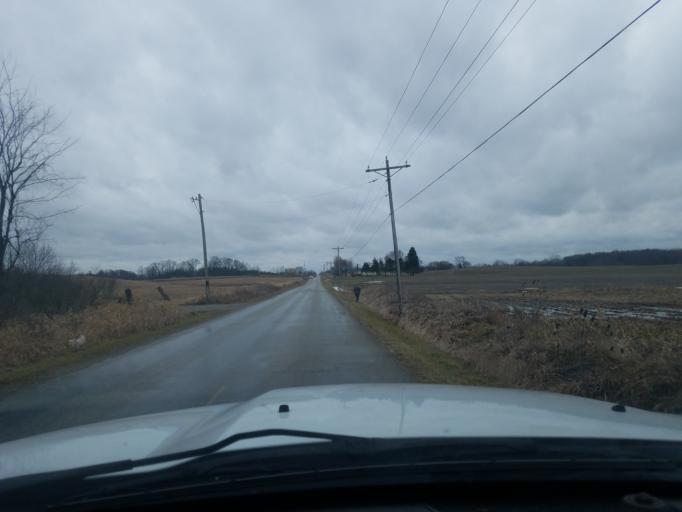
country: US
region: Indiana
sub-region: Noble County
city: Albion
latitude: 41.4195
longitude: -85.3956
